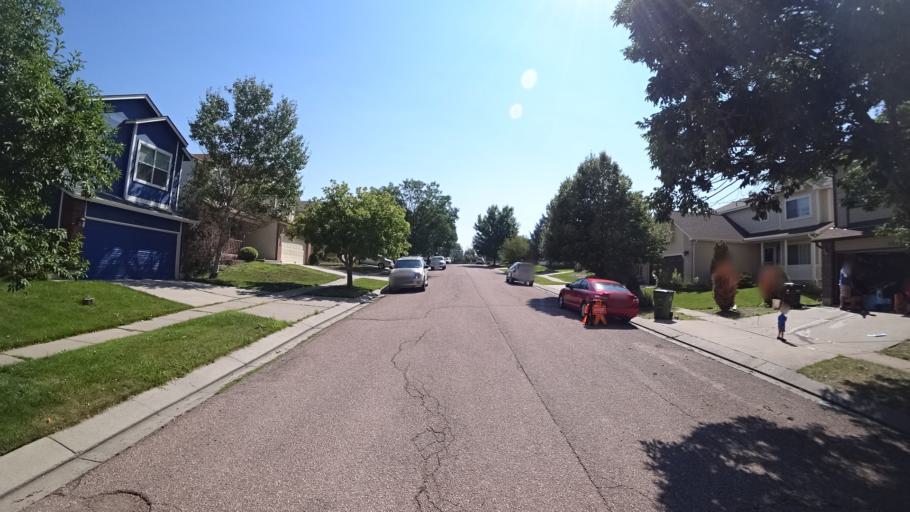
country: US
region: Colorado
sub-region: El Paso County
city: Air Force Academy
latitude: 38.9490
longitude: -104.7862
